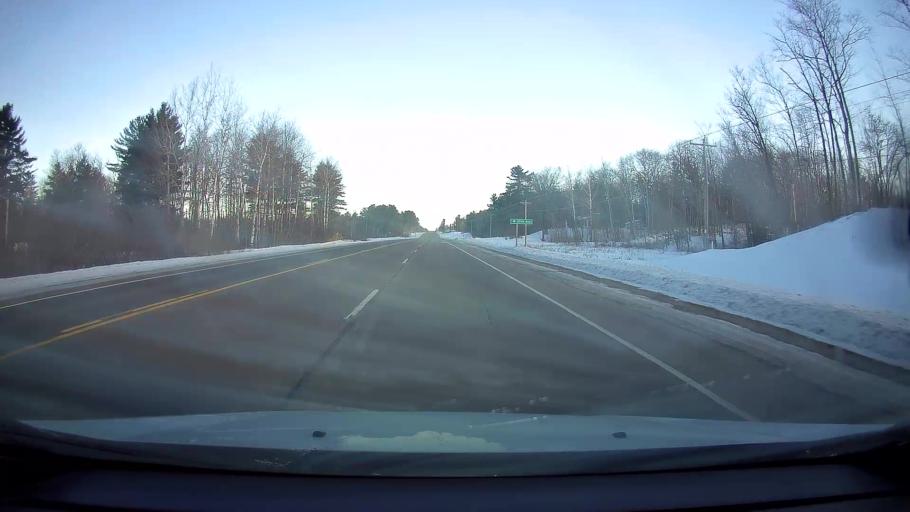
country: US
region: Wisconsin
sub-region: Barron County
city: Cumberland
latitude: 45.5652
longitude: -92.0173
